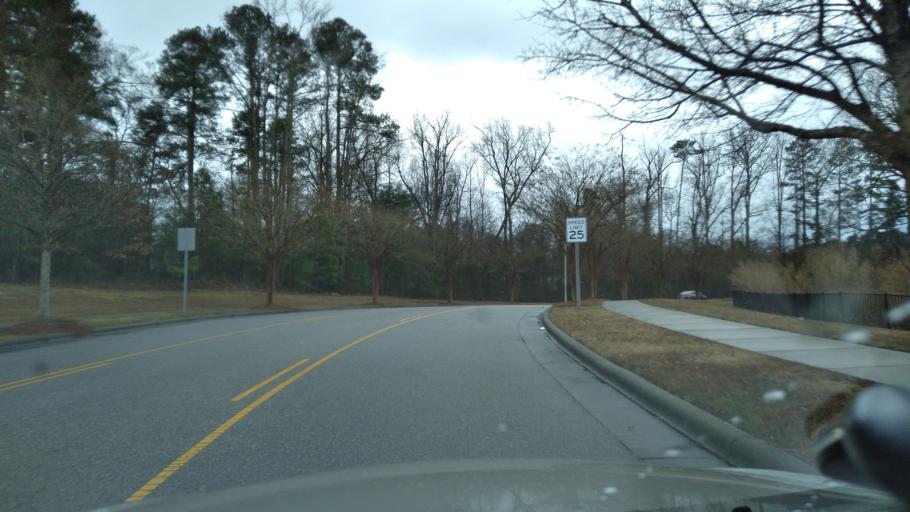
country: US
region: North Carolina
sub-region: Wake County
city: Knightdale
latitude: 35.7971
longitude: -78.5180
